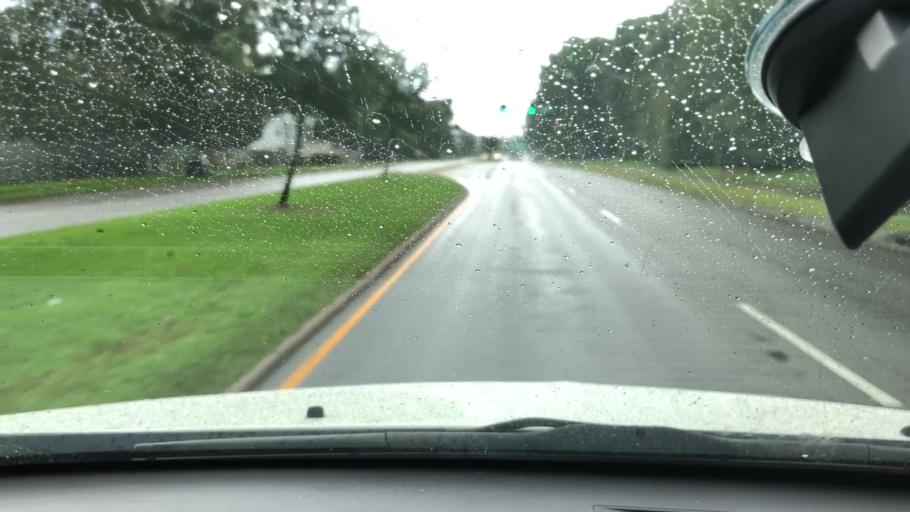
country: US
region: Virginia
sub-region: City of Chesapeake
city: Chesapeake
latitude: 36.8257
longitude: -76.1462
